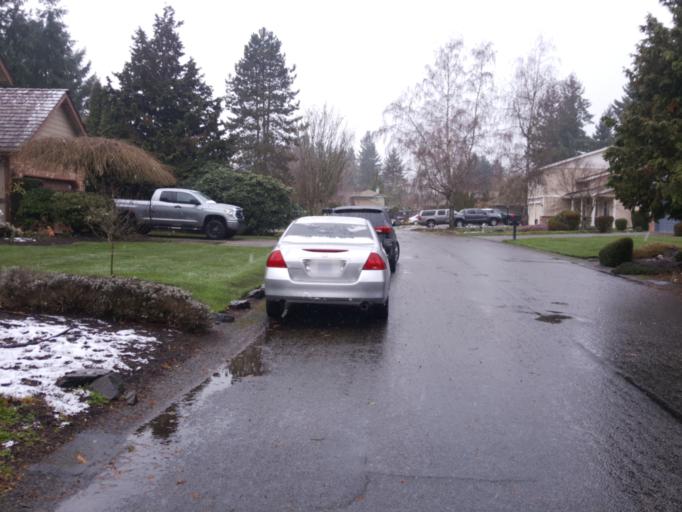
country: US
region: Washington
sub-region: Pierce County
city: Lakewood
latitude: 47.1978
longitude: -122.5454
